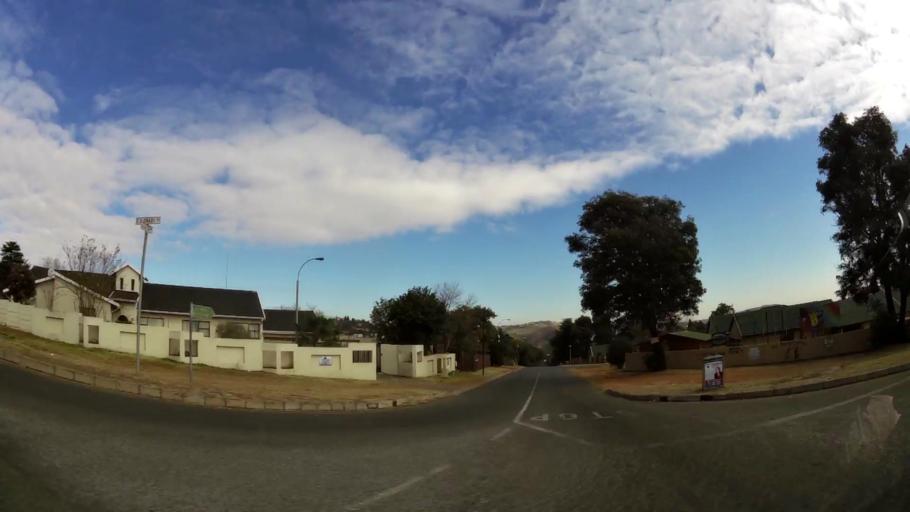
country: ZA
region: Gauteng
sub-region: City of Johannesburg Metropolitan Municipality
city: Roodepoort
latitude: -26.1161
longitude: 27.8512
